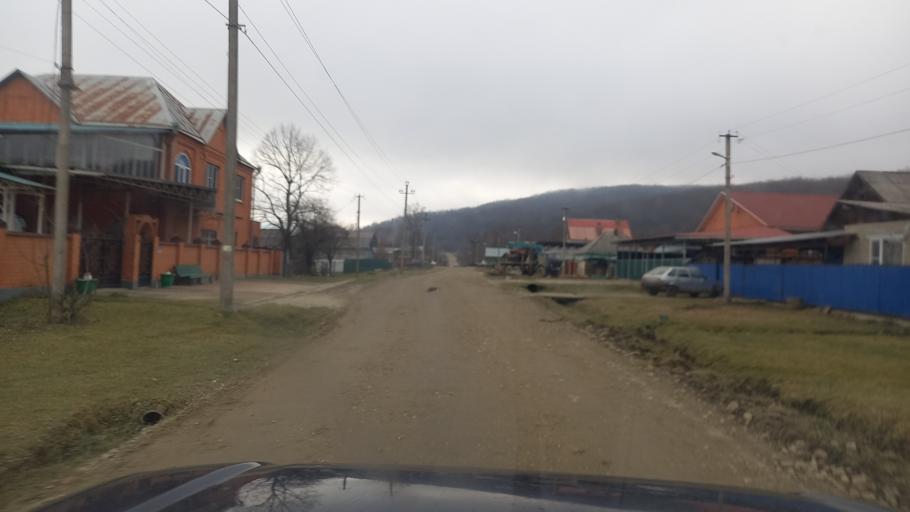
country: RU
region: Krasnodarskiy
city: Neftegorsk
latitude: 44.2493
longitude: 39.7579
